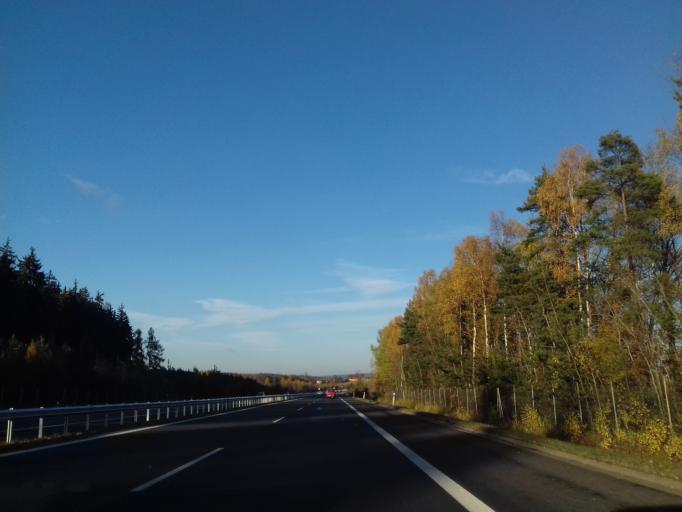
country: CZ
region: Plzensky
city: Myto
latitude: 49.8089
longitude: 13.7582
